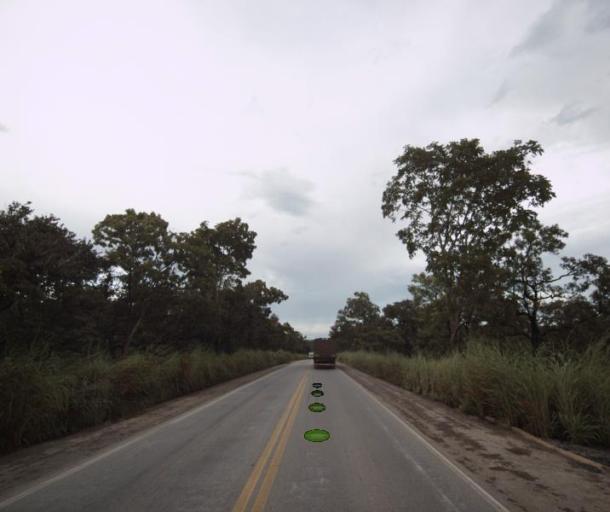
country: BR
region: Goias
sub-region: Porangatu
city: Porangatu
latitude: -13.6180
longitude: -49.0425
